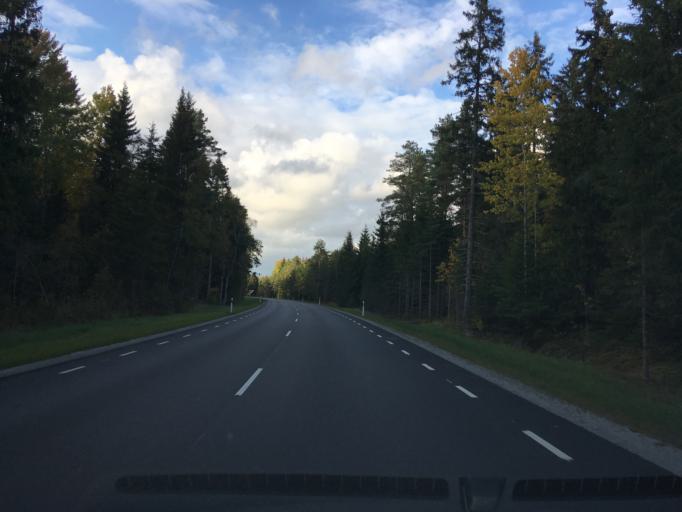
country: EE
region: Harju
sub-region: Nissi vald
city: Turba
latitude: 59.1480
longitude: 24.0782
